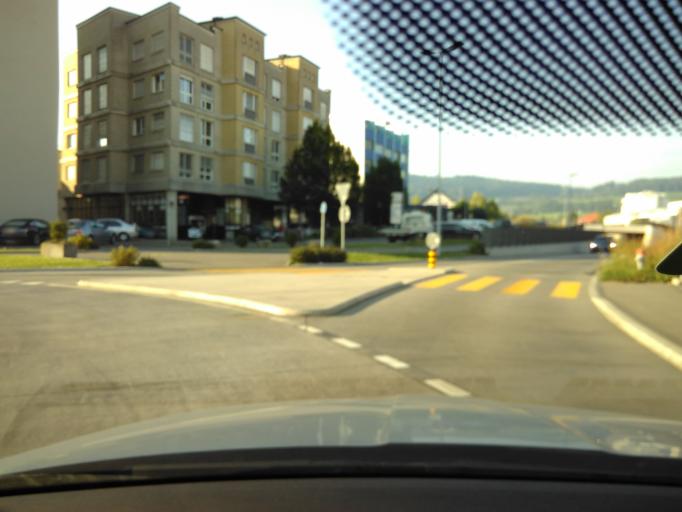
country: CH
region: Zurich
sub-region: Bezirk Dielsdorf
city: Regensdorf / Feldblumen-Riedthofstrasse
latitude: 47.4422
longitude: 8.4648
